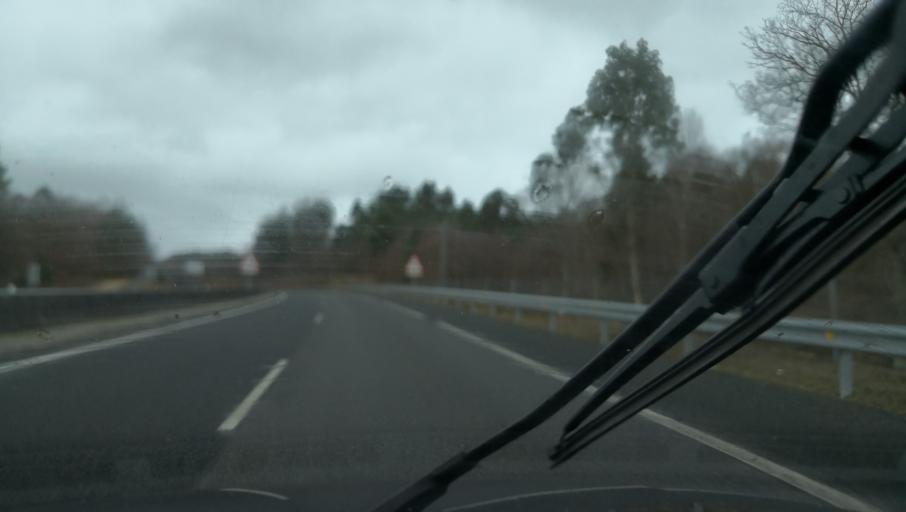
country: ES
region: Galicia
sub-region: Provincia de Pontevedra
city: Lalin
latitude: 42.6788
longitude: -8.1622
